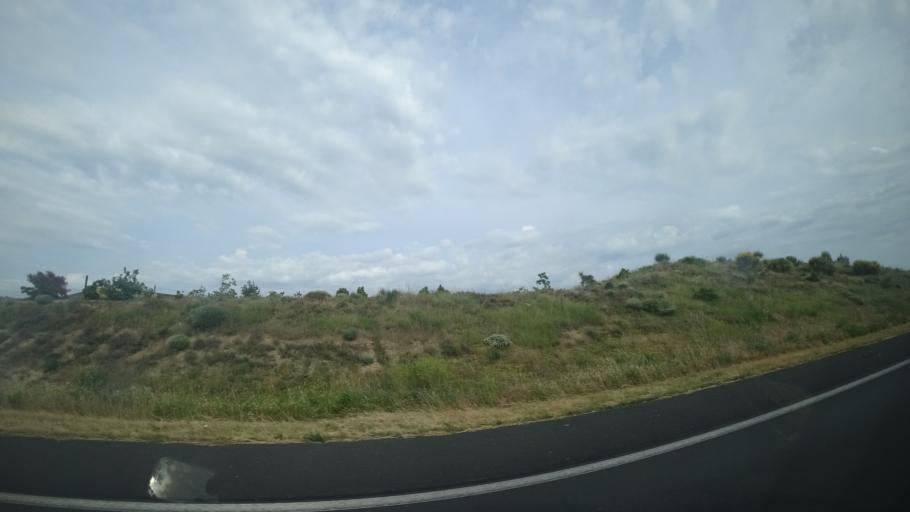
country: FR
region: Languedoc-Roussillon
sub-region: Departement de l'Herault
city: Paulhan
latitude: 43.5419
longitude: 3.4451
